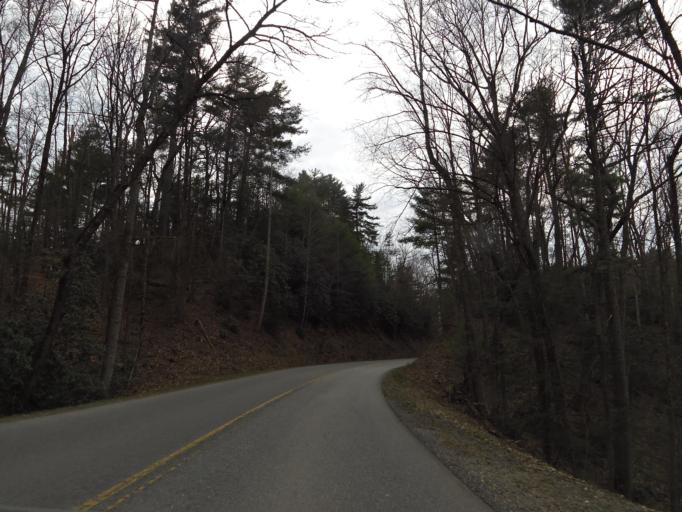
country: US
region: Tennessee
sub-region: Blount County
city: Wildwood
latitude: 35.6030
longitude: -83.7592
